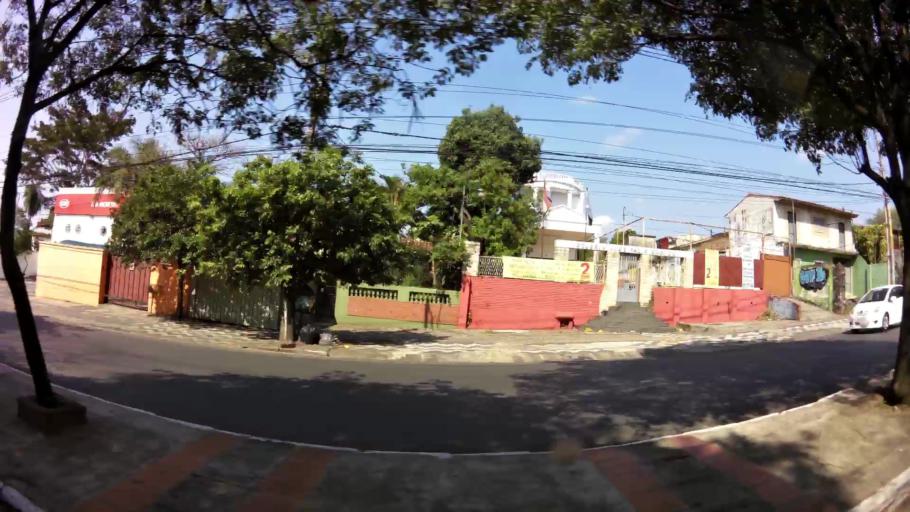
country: PY
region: Asuncion
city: Asuncion
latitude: -25.3168
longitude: -57.6299
